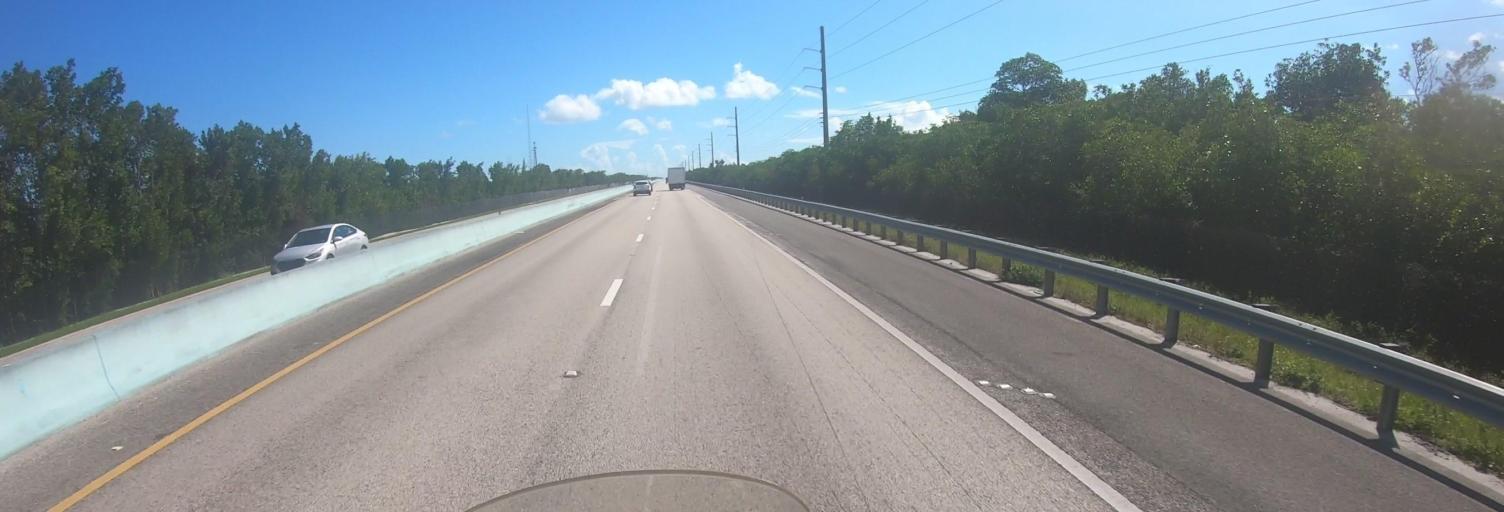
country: US
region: Florida
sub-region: Monroe County
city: North Key Largo
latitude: 25.2791
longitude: -80.4429
